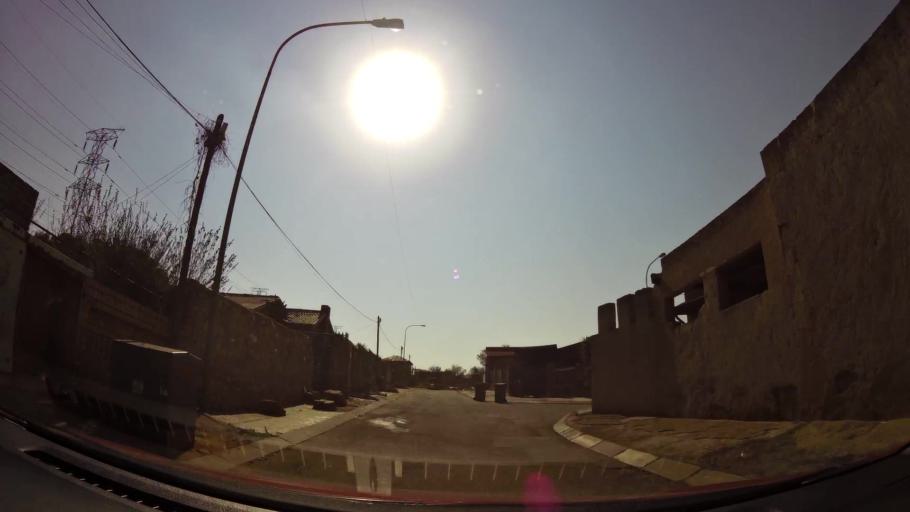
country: ZA
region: Gauteng
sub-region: City of Johannesburg Metropolitan Municipality
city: Soweto
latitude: -26.2507
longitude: 27.9342
